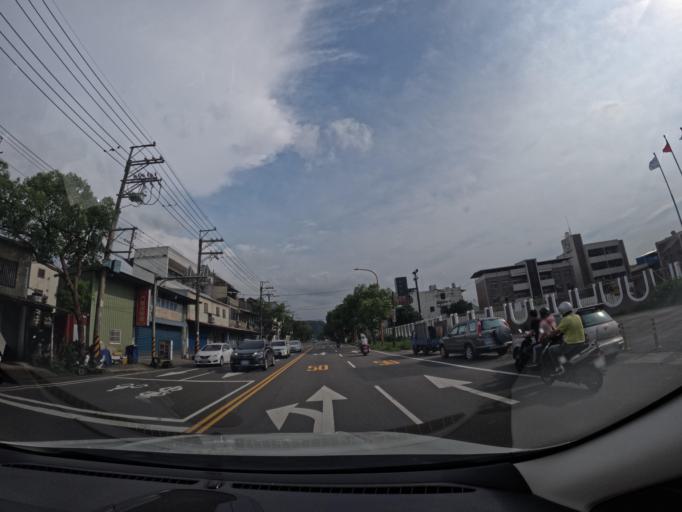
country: TW
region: Taiwan
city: Daxi
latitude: 24.8948
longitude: 121.3008
